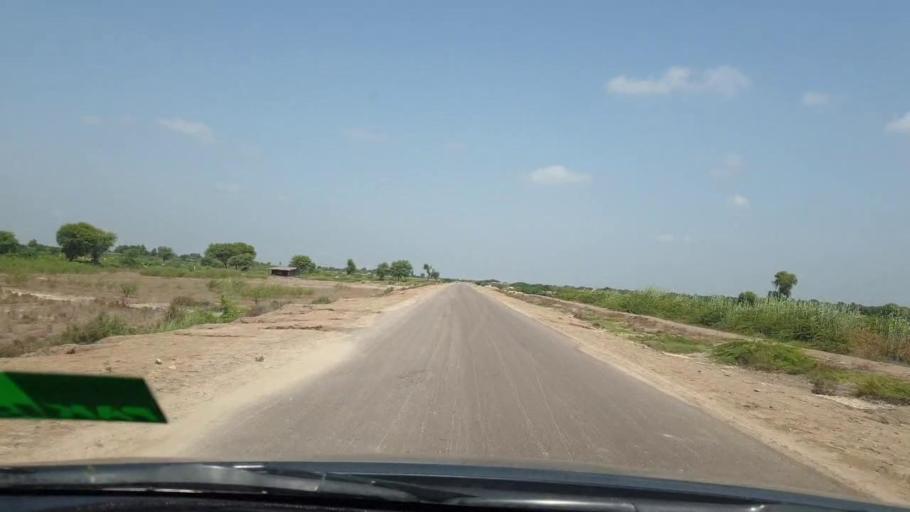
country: PK
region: Sindh
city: Digri
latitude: 24.9861
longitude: 69.1270
